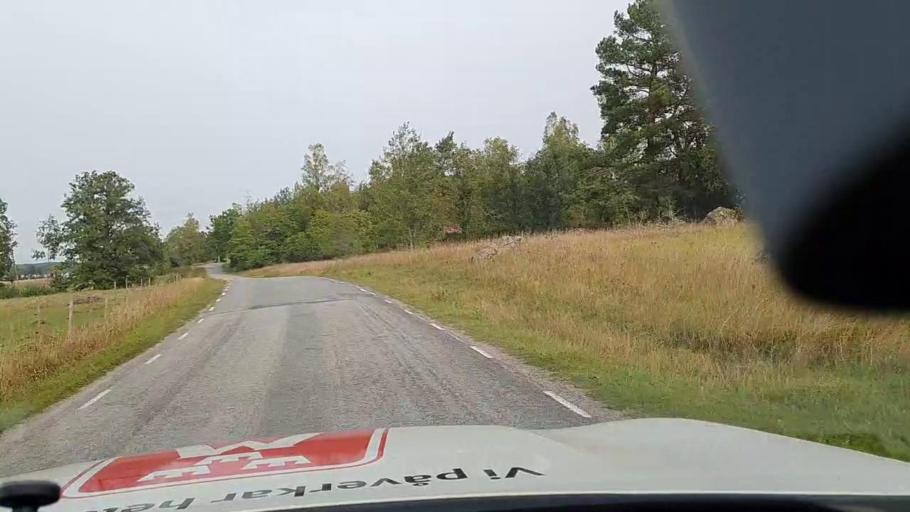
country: SE
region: Soedermanland
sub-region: Nykopings Kommun
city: Stigtomta
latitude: 58.9711
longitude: 16.9007
